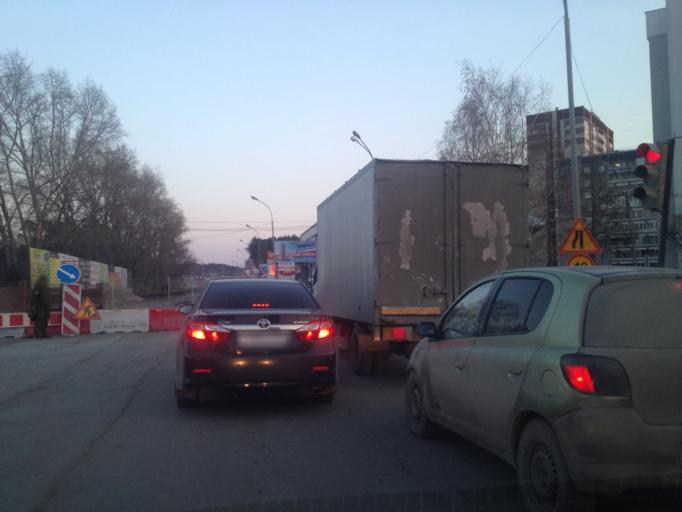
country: RU
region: Sverdlovsk
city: Yekaterinburg
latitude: 56.7983
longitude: 60.5952
